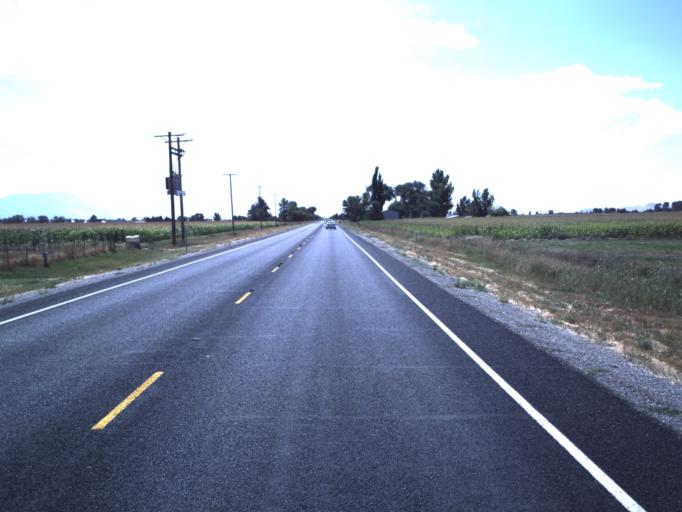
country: US
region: Utah
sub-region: Box Elder County
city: Garland
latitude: 41.7810
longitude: -112.1493
